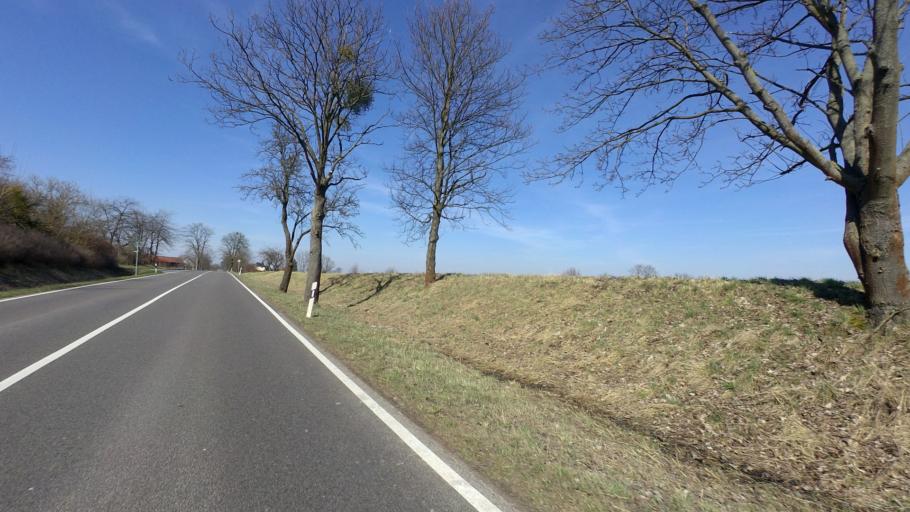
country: DE
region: Brandenburg
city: Protzel
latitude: 52.5978
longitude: 14.0254
